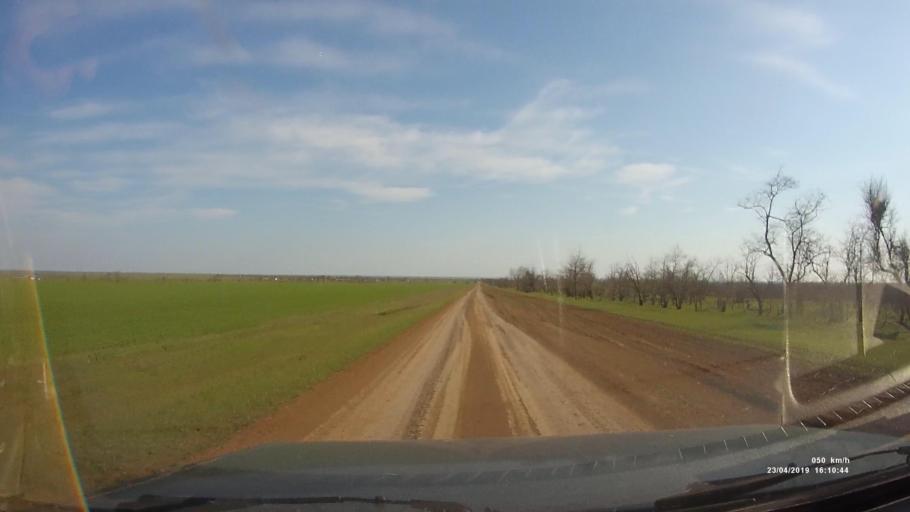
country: RU
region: Rostov
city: Remontnoye
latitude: 46.4798
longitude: 43.1231
